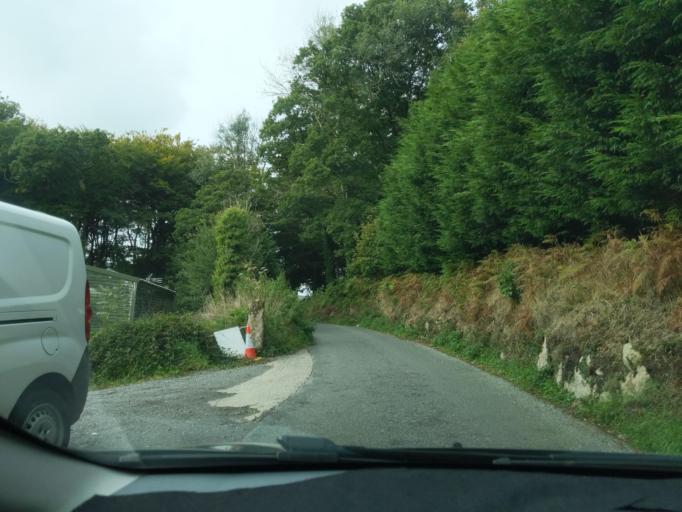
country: GB
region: England
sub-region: Cornwall
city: Lostwithiel
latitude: 50.3997
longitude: -4.6931
